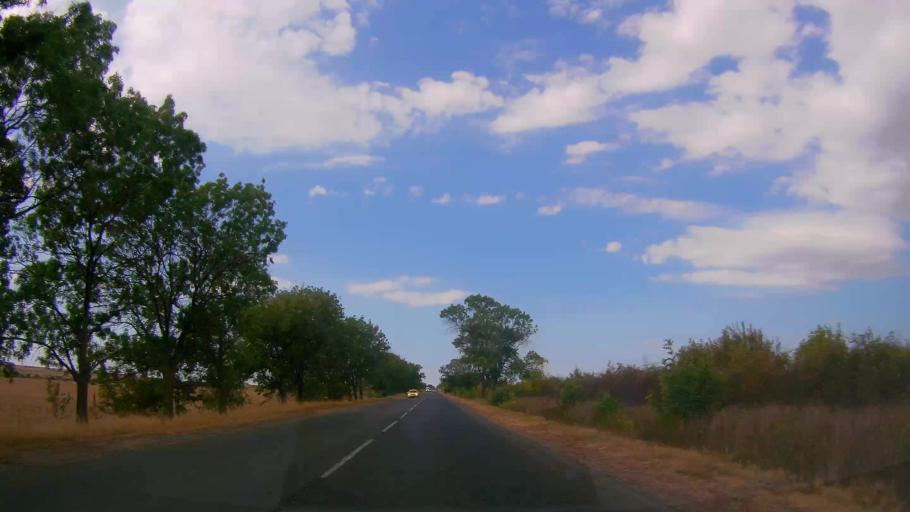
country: BG
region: Burgas
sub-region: Obshtina Aytos
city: Aytos
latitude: 42.6943
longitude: 27.1768
